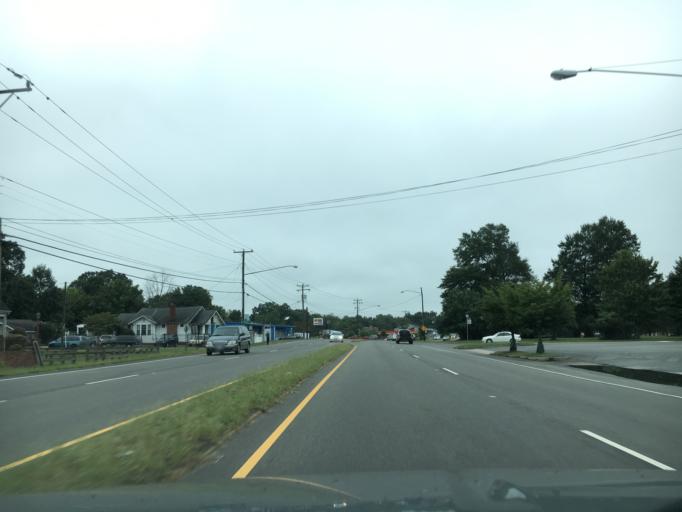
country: US
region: Virginia
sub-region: Chesterfield County
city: Bensley
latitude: 37.4885
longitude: -77.4943
